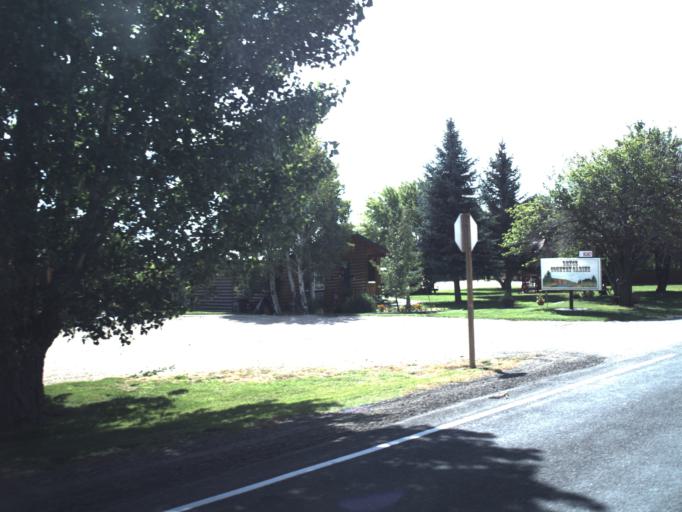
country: US
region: Utah
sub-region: Garfield County
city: Panguitch
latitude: 37.6291
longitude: -112.0819
